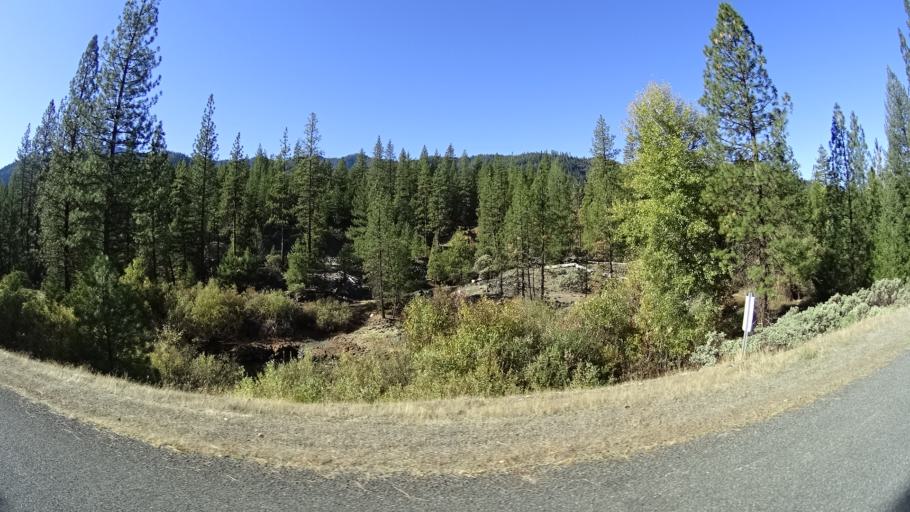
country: US
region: California
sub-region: Trinity County
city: Weaverville
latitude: 41.1170
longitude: -123.0916
